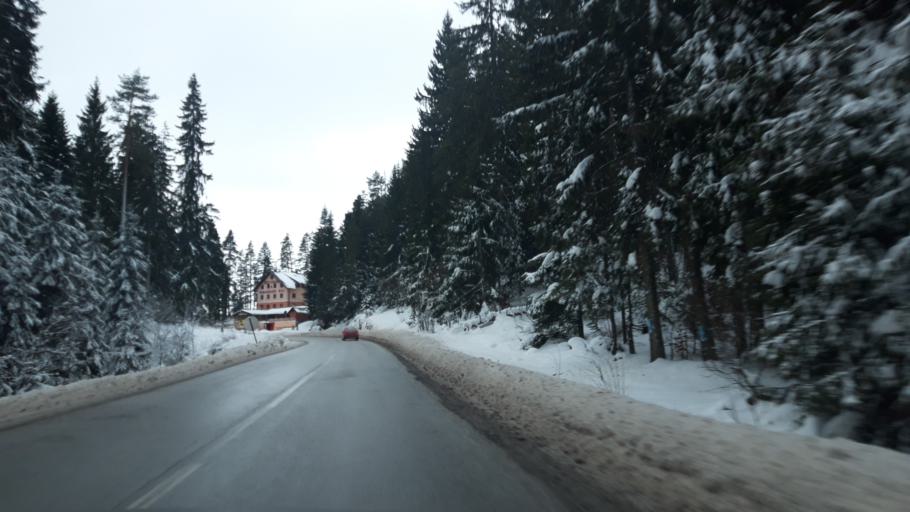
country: BA
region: Republika Srpska
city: Pale
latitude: 43.9235
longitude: 18.6526
